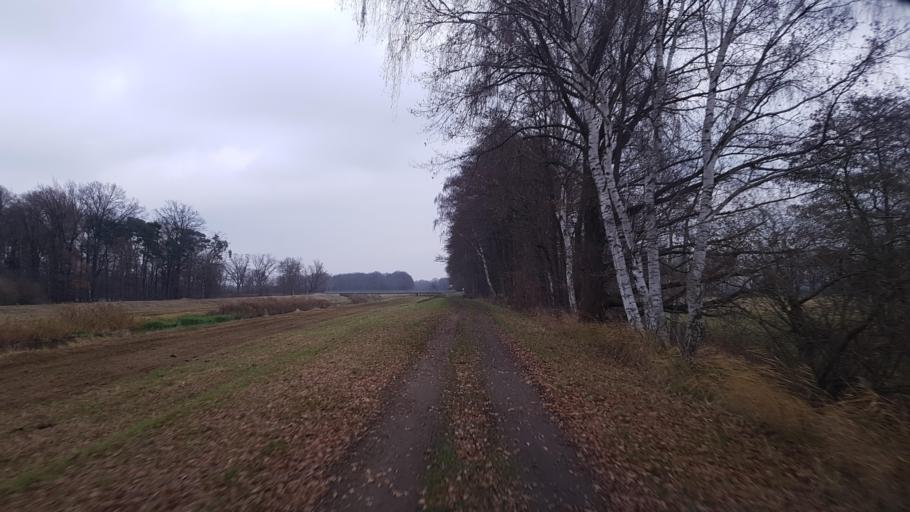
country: DE
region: Brandenburg
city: Schraden
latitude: 51.4593
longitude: 13.7071
